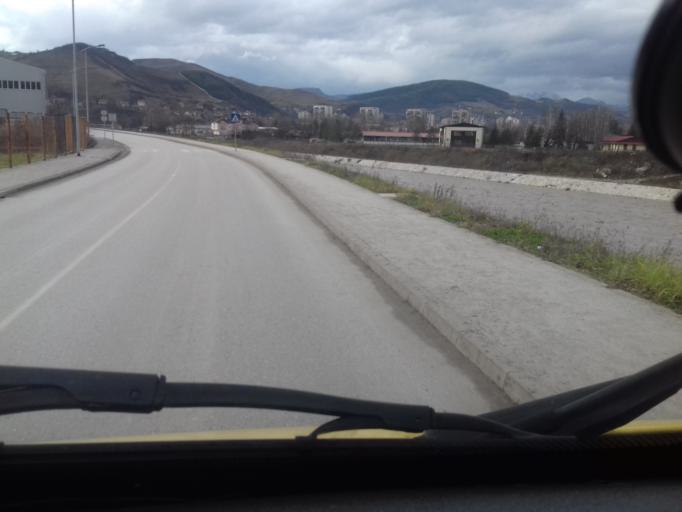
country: BA
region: Federation of Bosnia and Herzegovina
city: Zenica
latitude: 44.1902
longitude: 17.9325
